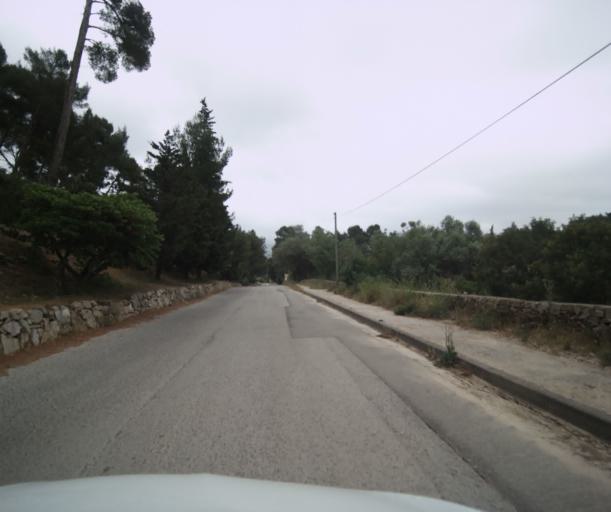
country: FR
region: Provence-Alpes-Cote d'Azur
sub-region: Departement du Var
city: Ollioules
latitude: 43.1470
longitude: 5.8778
